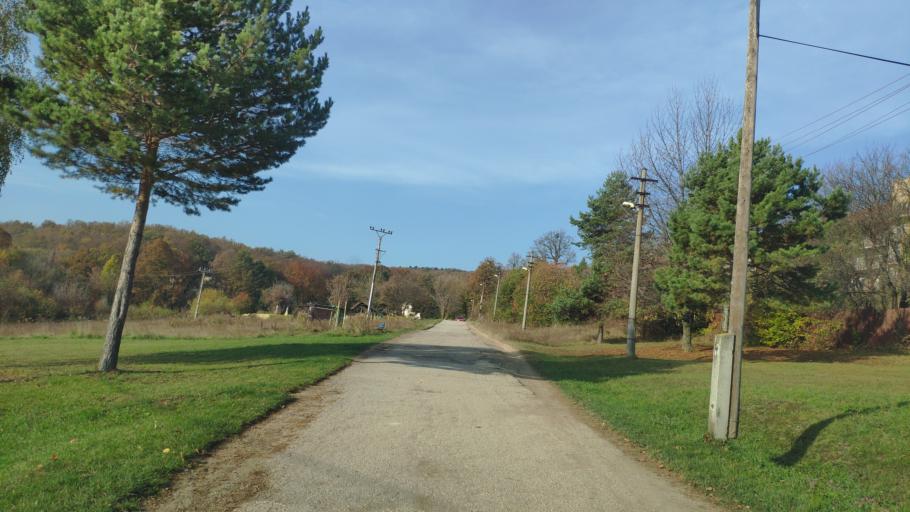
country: SK
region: Kosicky
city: Kosice
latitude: 48.7444
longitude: 21.2138
